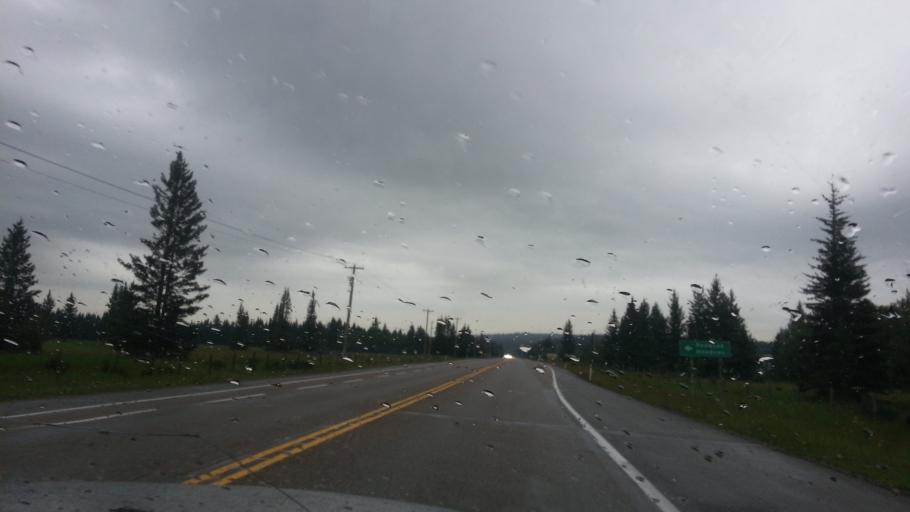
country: CA
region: Alberta
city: Cochrane
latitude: 50.9756
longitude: -114.5250
